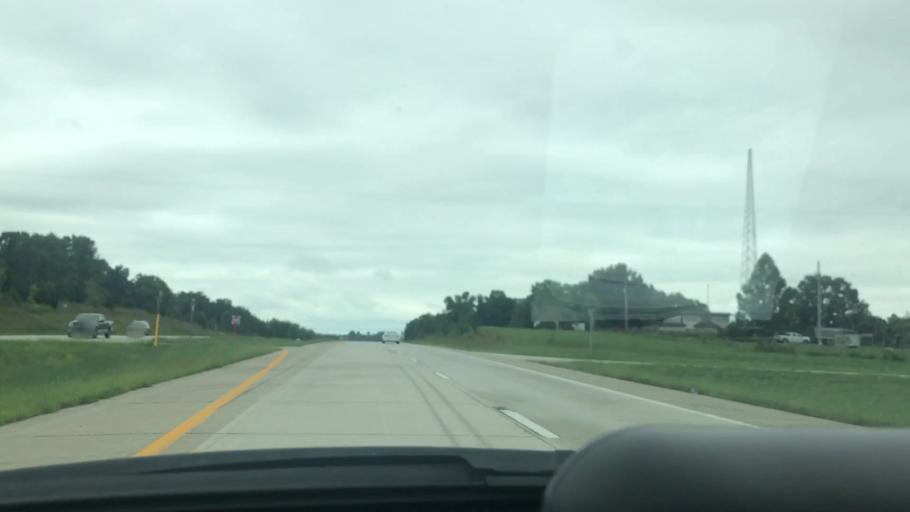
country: US
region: Missouri
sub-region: Dallas County
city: Buffalo
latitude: 37.5392
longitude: -93.1375
